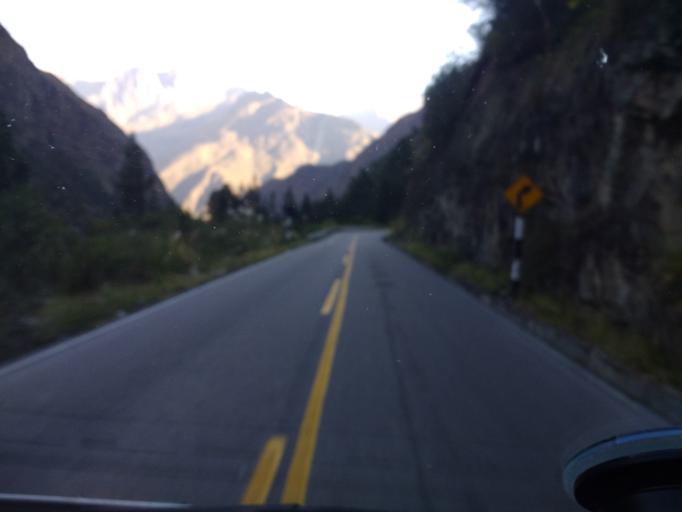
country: PE
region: Cusco
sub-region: Provincia de Urubamba
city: Ollantaytambo
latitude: -13.2001
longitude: -72.2960
